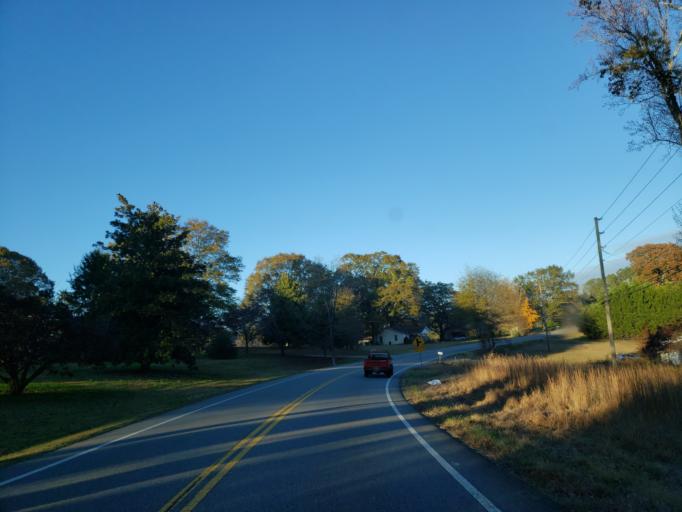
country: US
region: Georgia
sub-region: Cherokee County
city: Canton
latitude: 34.1976
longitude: -84.4214
